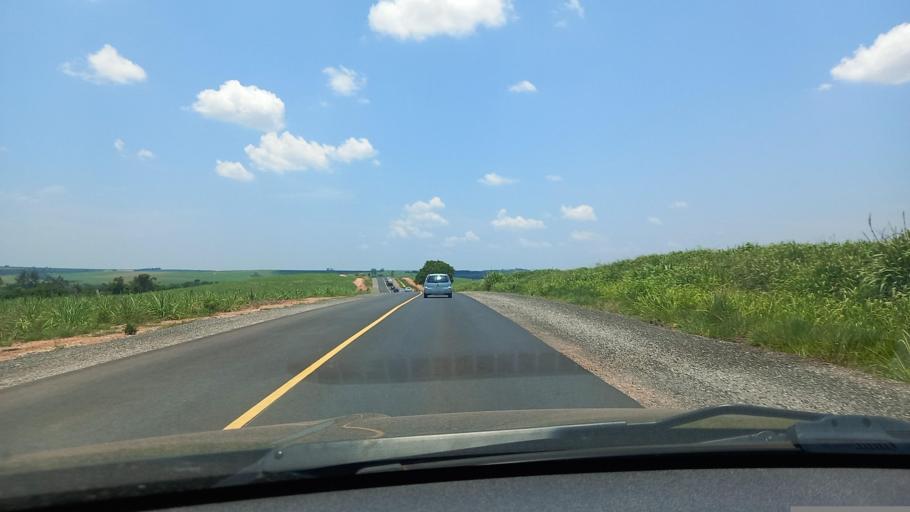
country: BR
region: Sao Paulo
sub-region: Moji-Guacu
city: Mogi-Gaucu
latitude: -22.3671
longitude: -46.8730
